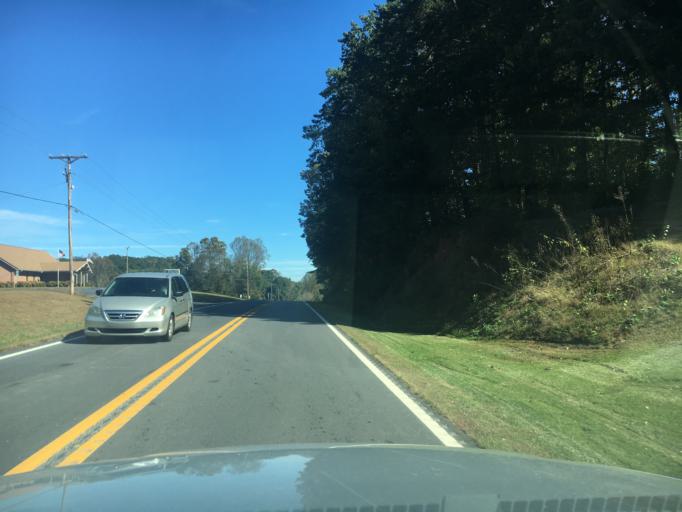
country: US
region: North Carolina
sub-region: Burke County
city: Salem
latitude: 35.6597
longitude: -81.7531
